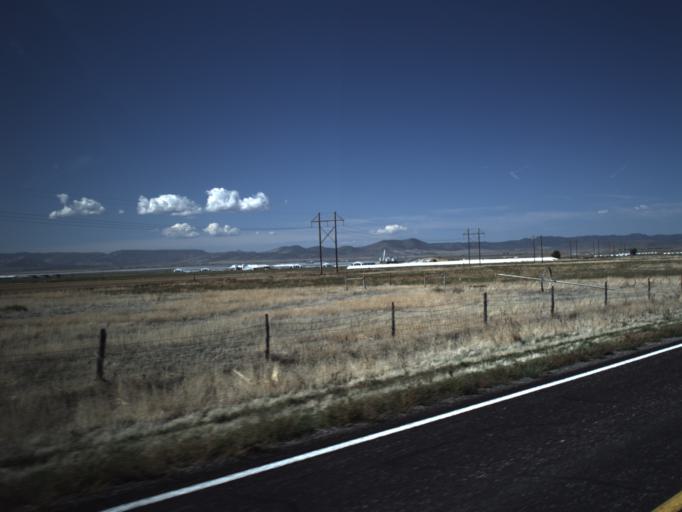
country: US
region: Utah
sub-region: Washington County
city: Enterprise
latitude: 37.6730
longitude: -113.5545
